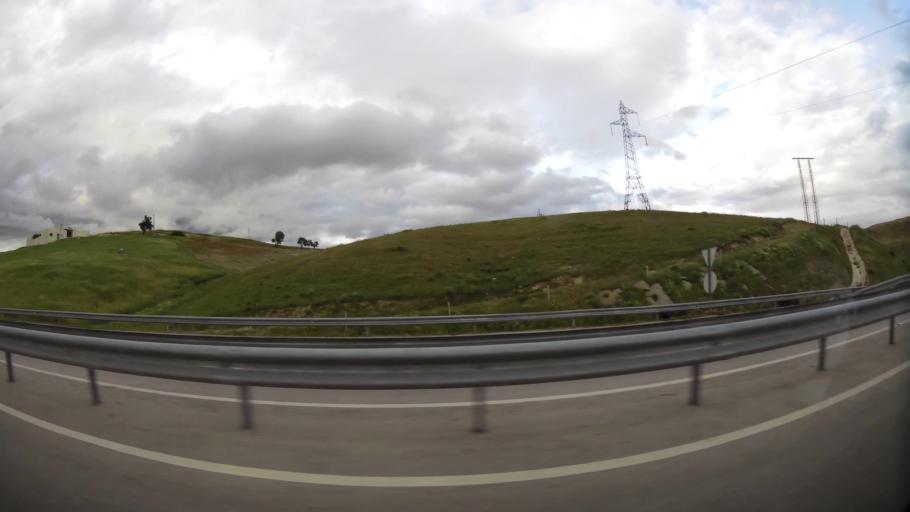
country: MA
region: Taza-Al Hoceima-Taounate
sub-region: Taza
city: Taza
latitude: 34.2620
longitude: -3.9560
